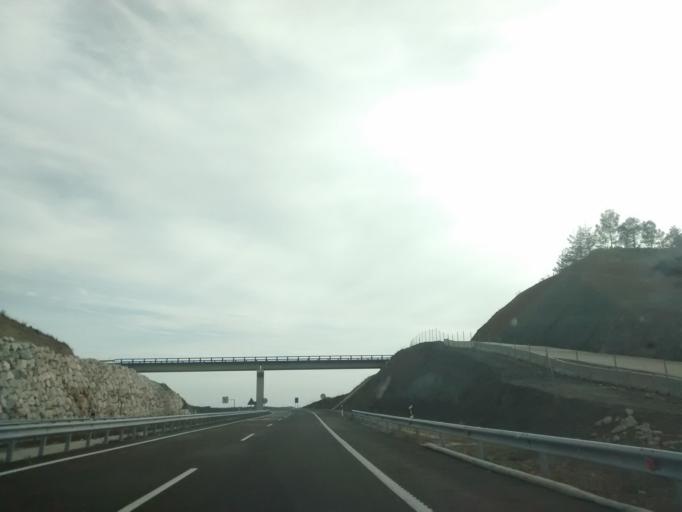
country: ES
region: Aragon
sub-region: Provincia de Zaragoza
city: Undues de Lerda
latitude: 42.6228
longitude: -1.1198
